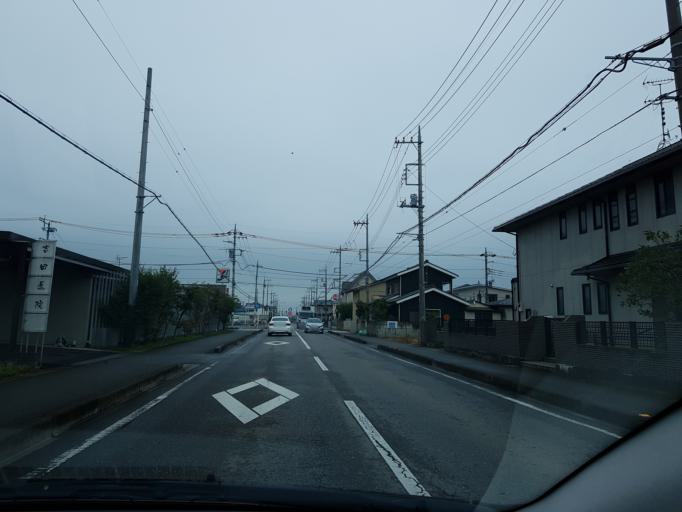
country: JP
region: Tochigi
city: Utsunomiya-shi
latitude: 36.5853
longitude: 139.9039
